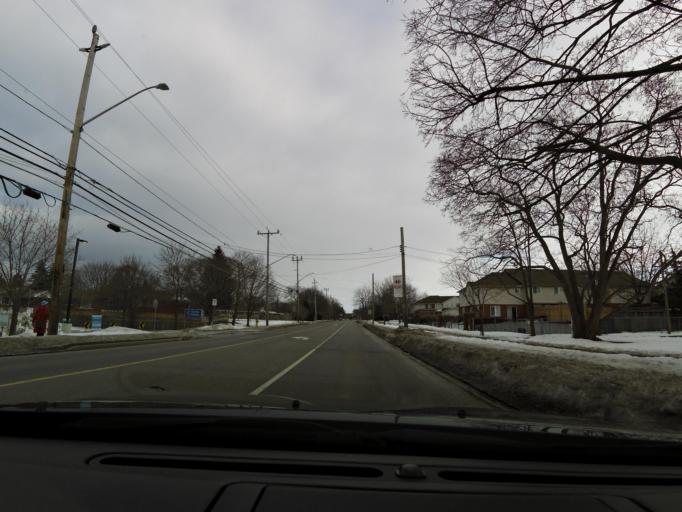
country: CA
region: Ontario
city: Oakville
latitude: 43.1874
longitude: -79.5419
